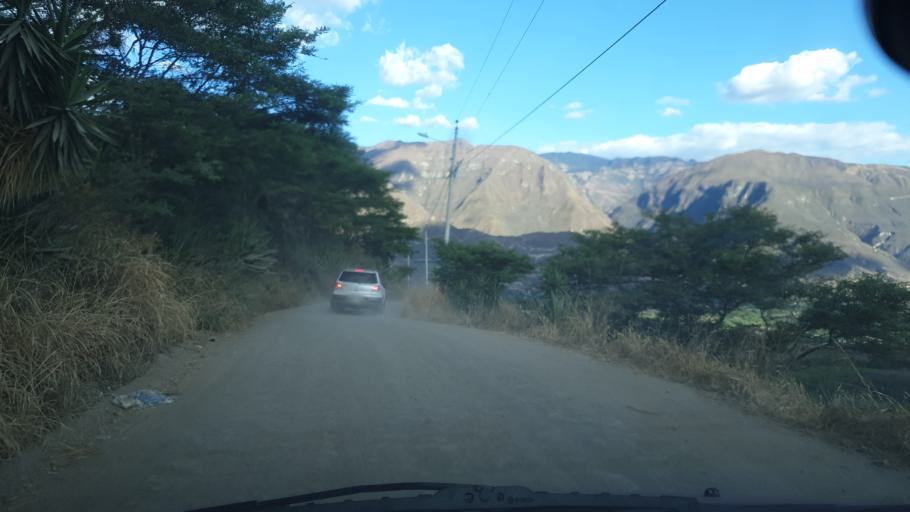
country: EC
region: Azuay
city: Cuenca
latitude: -3.2854
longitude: -79.2966
